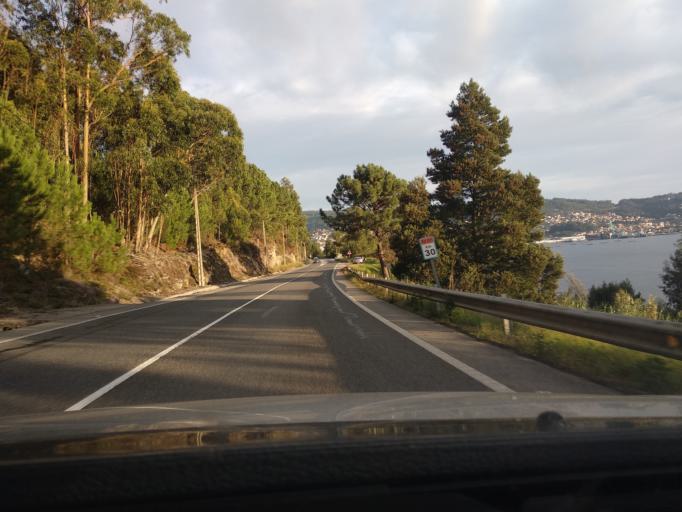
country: ES
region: Galicia
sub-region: Provincia de Pontevedra
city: Moana
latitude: 42.2826
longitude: -8.6979
